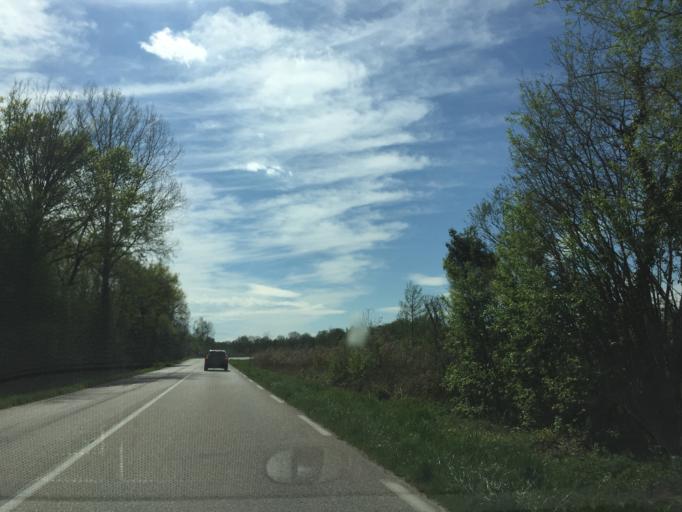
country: FR
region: Rhone-Alpes
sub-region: Departement de l'Isere
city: Sermerieu
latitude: 45.6902
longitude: 5.3862
